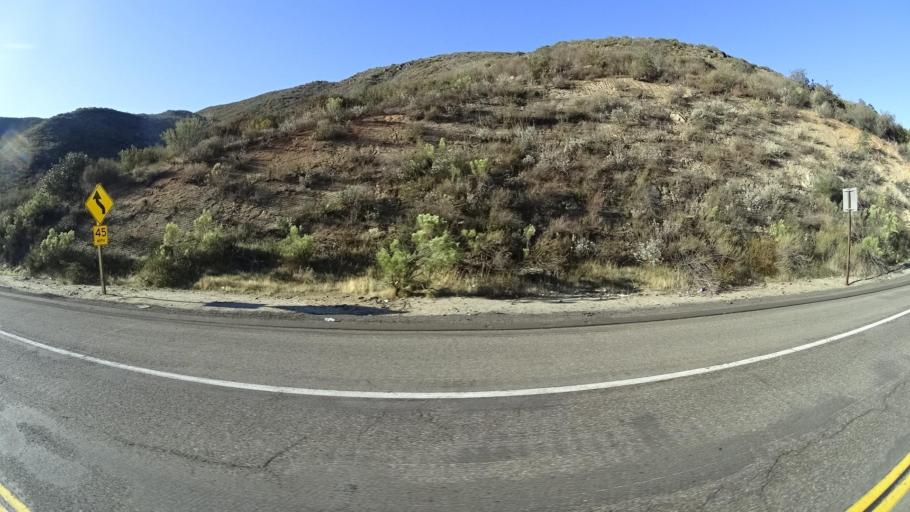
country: MX
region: Baja California
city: Tecate
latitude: 32.5965
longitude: -116.6531
